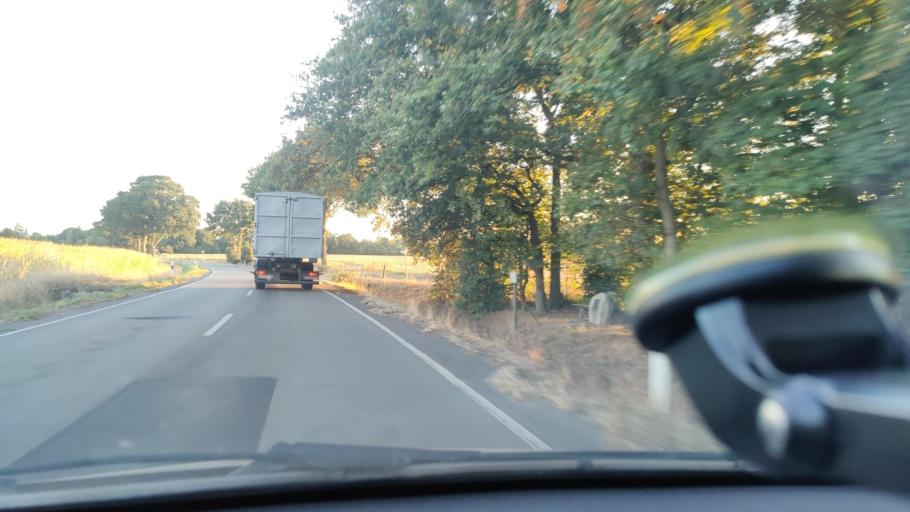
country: DE
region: North Rhine-Westphalia
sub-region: Regierungsbezirk Munster
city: Klein Reken
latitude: 51.7711
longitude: 7.0004
